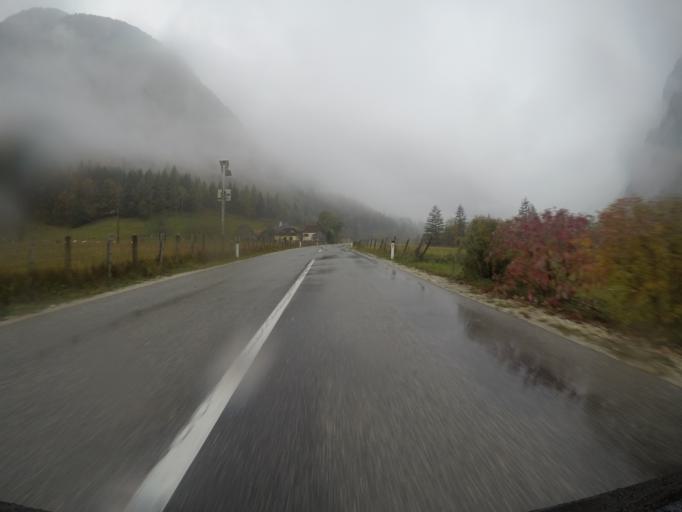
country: SI
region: Kranjska Gora
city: Kranjska Gora
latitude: 46.3746
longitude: 13.7521
